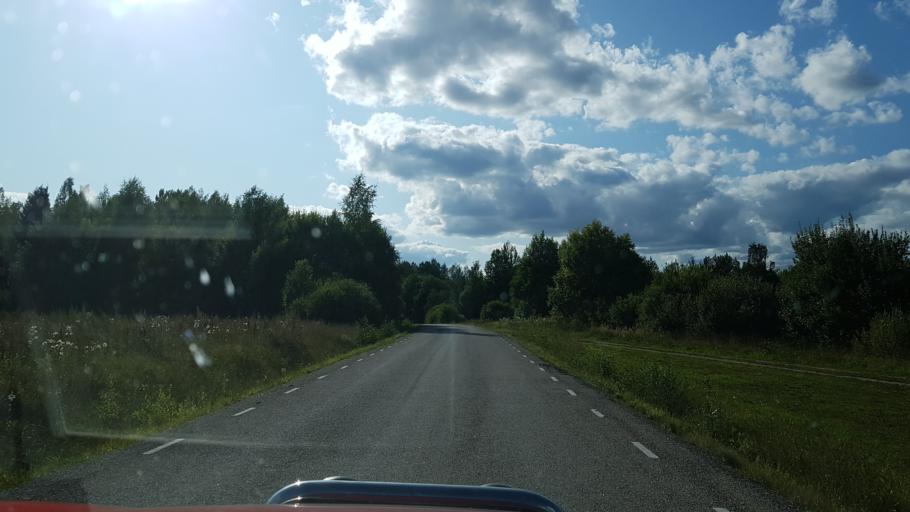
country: EE
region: Vorumaa
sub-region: Voru linn
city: Voru
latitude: 57.9281
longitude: 27.0598
